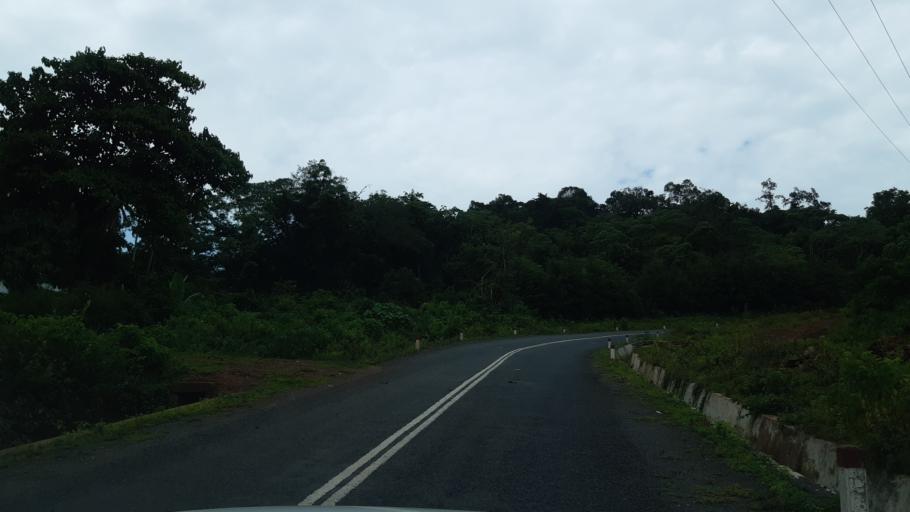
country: ET
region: Southern Nations, Nationalities, and People's Region
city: Bonga
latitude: 7.1993
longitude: 36.2884
